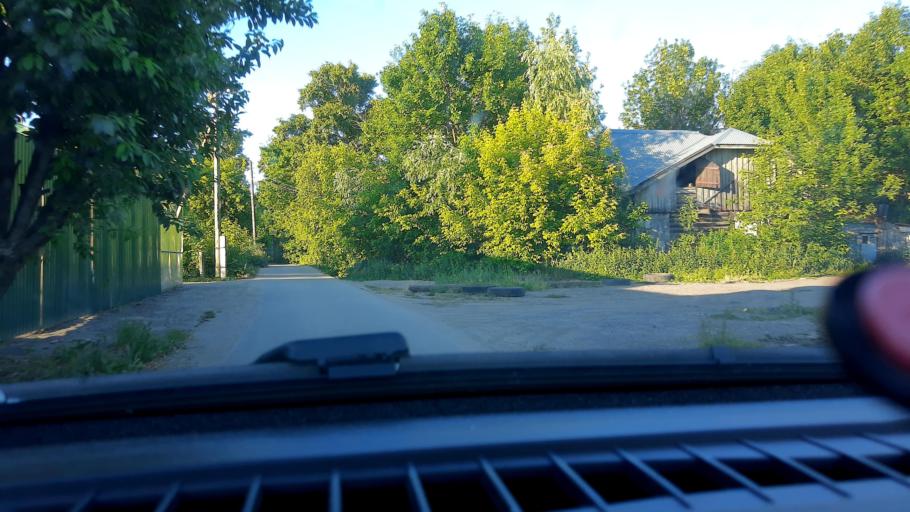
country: RU
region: Nizjnij Novgorod
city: Nizhniy Novgorod
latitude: 56.3136
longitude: 43.9273
